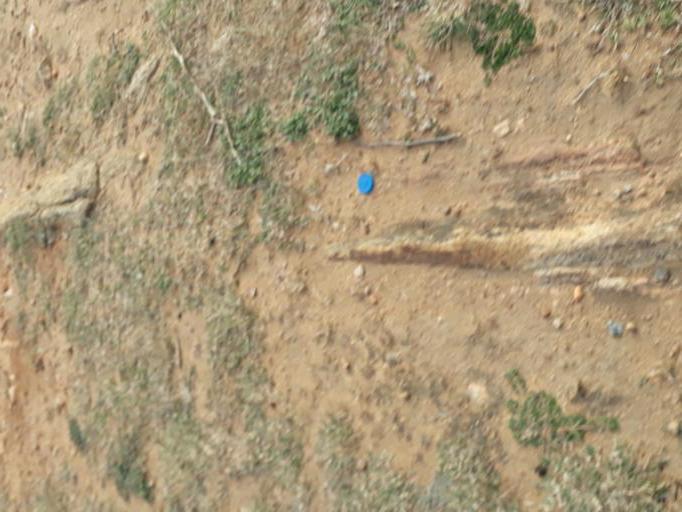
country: IN
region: Karnataka
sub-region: Mandya
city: Melukote
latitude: 12.6578
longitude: 76.6473
